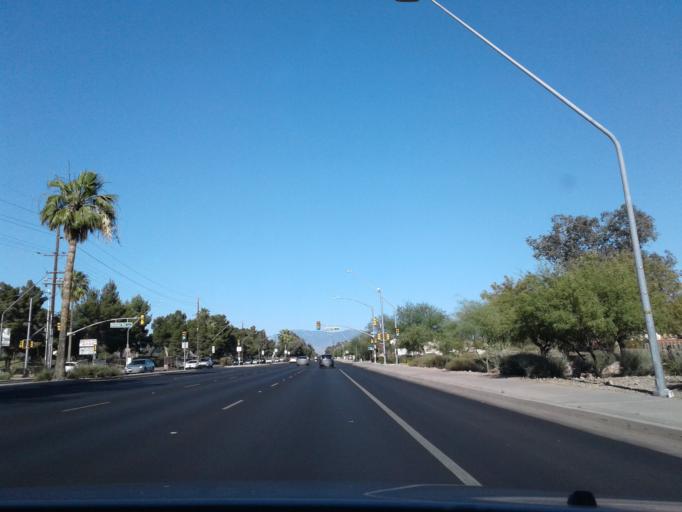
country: US
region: Arizona
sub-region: Pima County
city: Tucson
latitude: 32.2069
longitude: -110.9191
